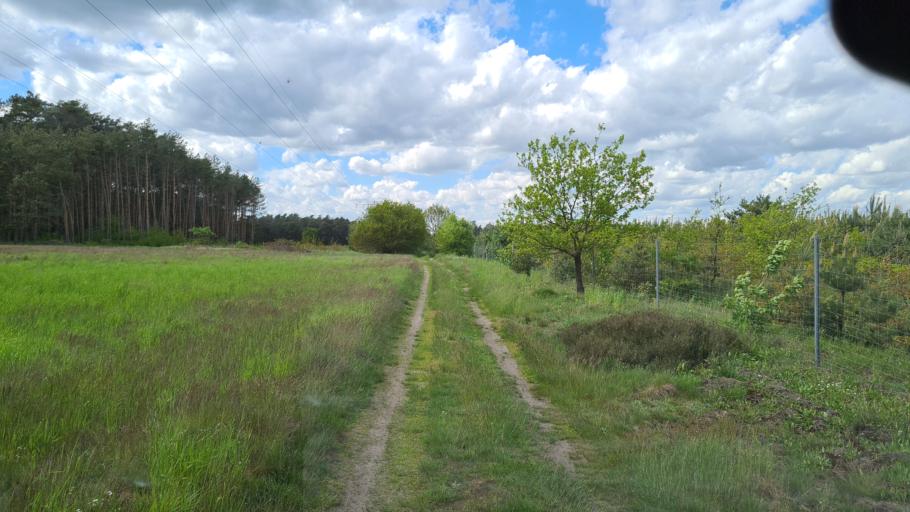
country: DE
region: Brandenburg
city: Crinitz
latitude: 51.7164
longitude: 13.7744
